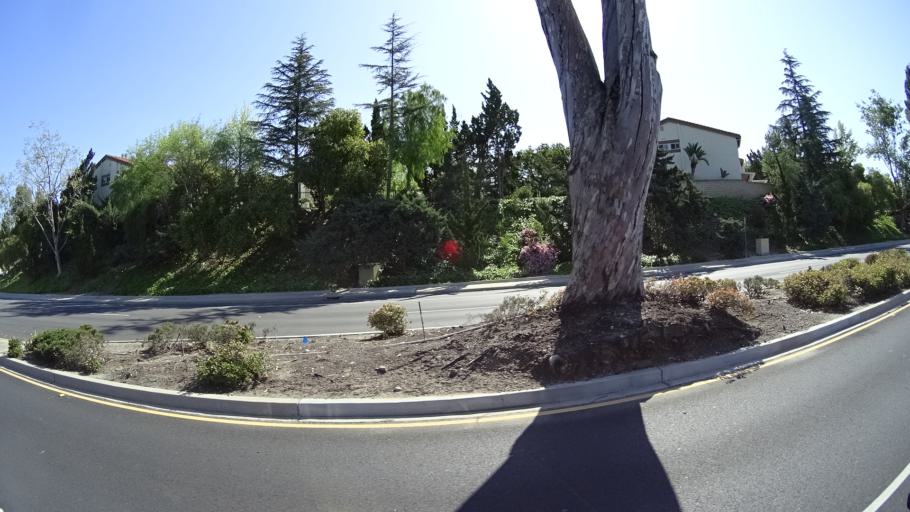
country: US
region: California
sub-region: Ventura County
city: Casa Conejo
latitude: 34.1925
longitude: -118.8941
